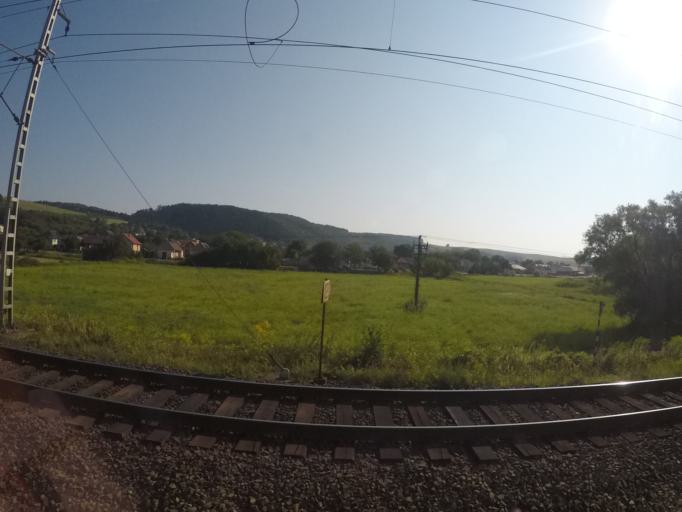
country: SK
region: Kosicky
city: Kosice
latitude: 48.8018
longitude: 21.2404
